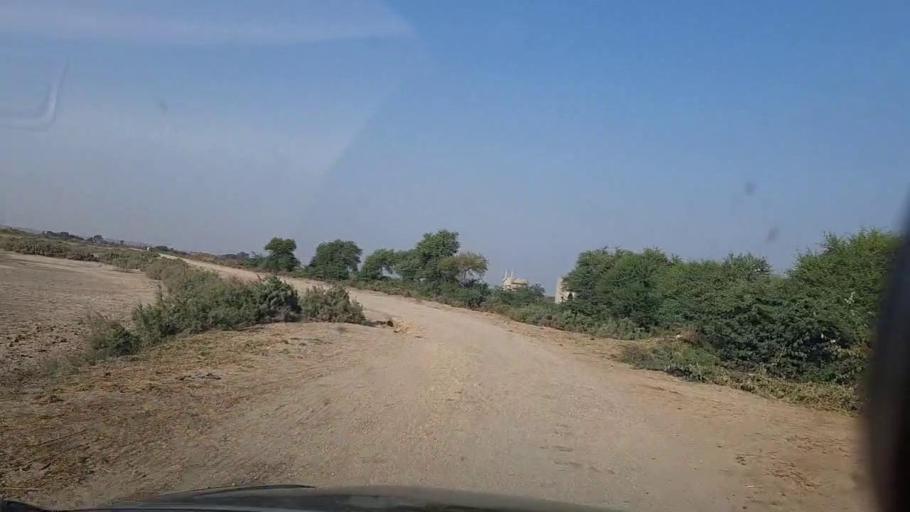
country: PK
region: Sindh
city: Thatta
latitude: 24.5950
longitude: 67.8749
